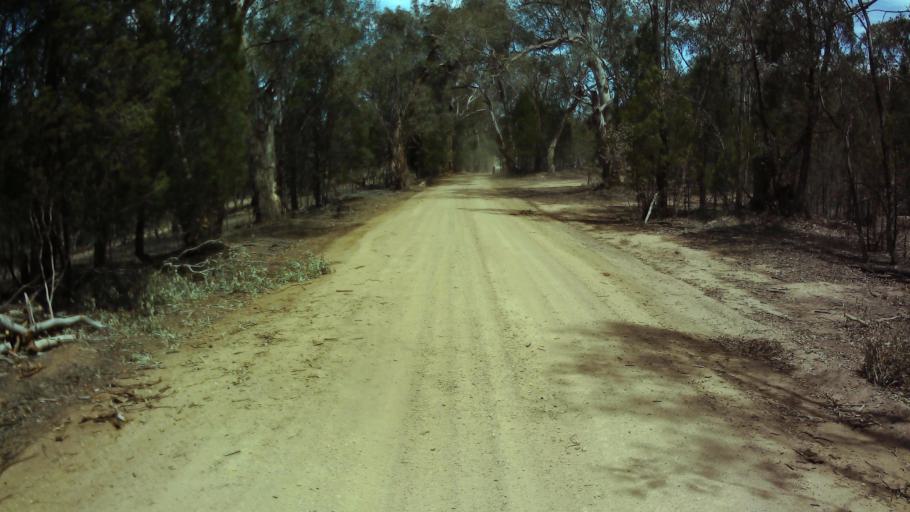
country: AU
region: New South Wales
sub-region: Weddin
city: Grenfell
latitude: -33.8184
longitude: 148.1665
